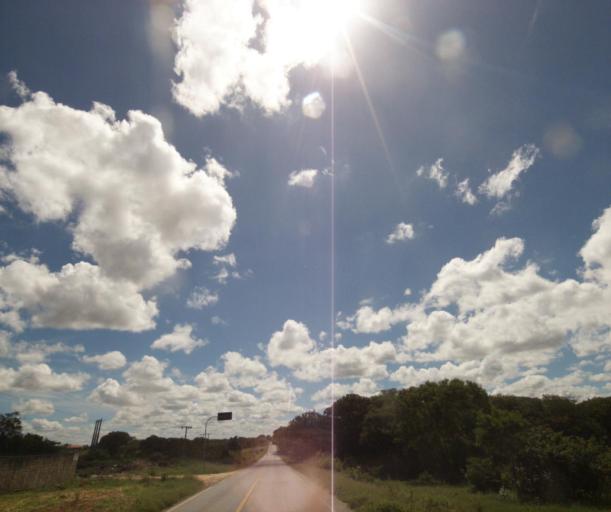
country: BR
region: Bahia
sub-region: Sao Felix Do Coribe
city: Santa Maria da Vitoria
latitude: -13.4085
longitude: -44.1837
